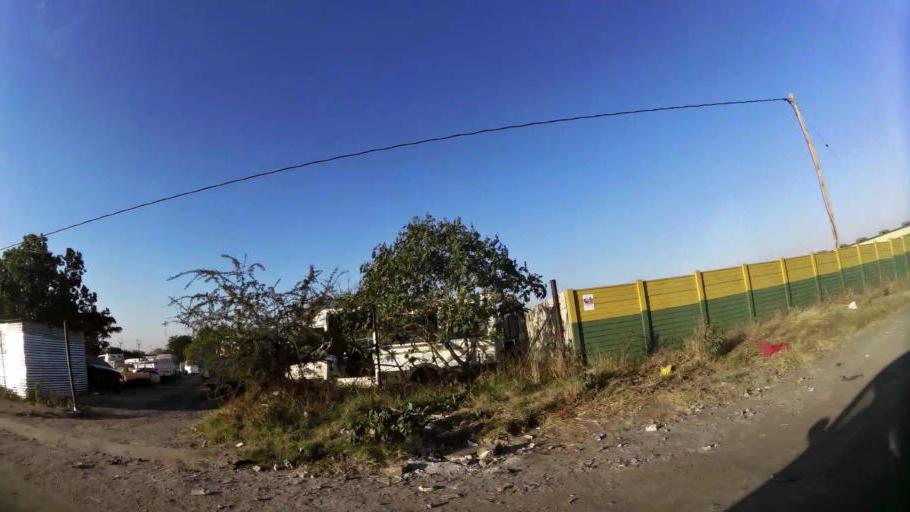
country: ZA
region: North-West
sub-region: Bojanala Platinum District Municipality
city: Rustenburg
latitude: -25.6302
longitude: 27.2195
